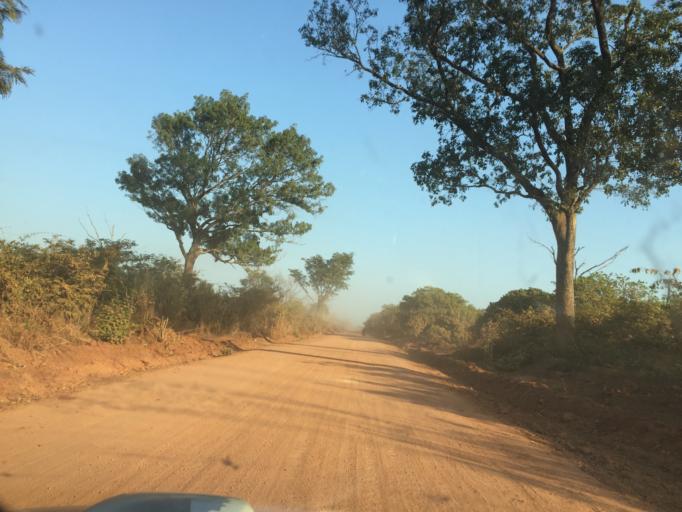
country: GW
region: Oio
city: Farim
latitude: 12.5308
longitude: -15.2729
